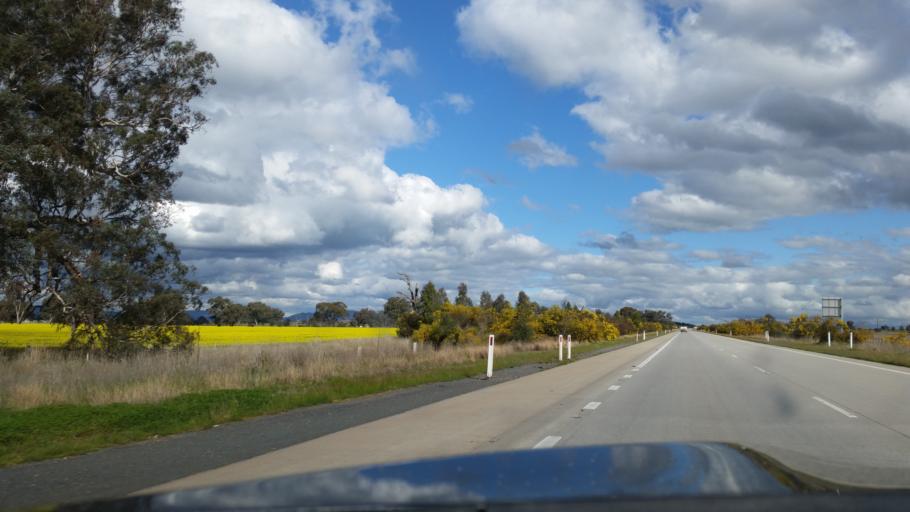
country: AU
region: New South Wales
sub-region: Greater Hume Shire
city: Jindera
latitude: -35.9461
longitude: 147.0039
